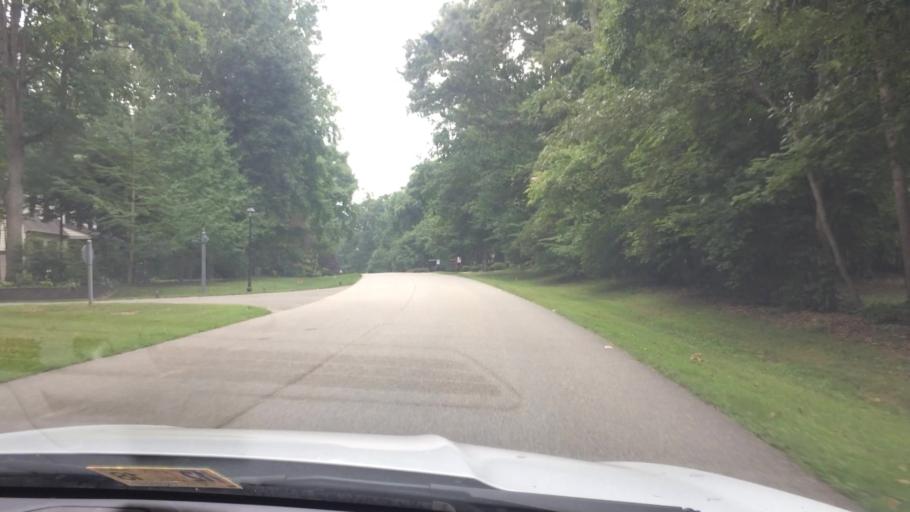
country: US
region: Virginia
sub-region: James City County
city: Williamsburg
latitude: 37.3068
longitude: -76.7712
